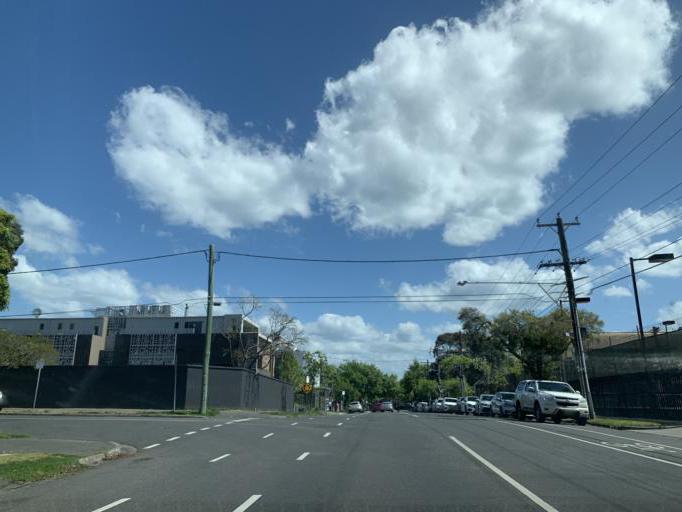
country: AU
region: Victoria
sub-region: Bayside
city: North Brighton
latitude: -37.9116
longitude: 144.9939
